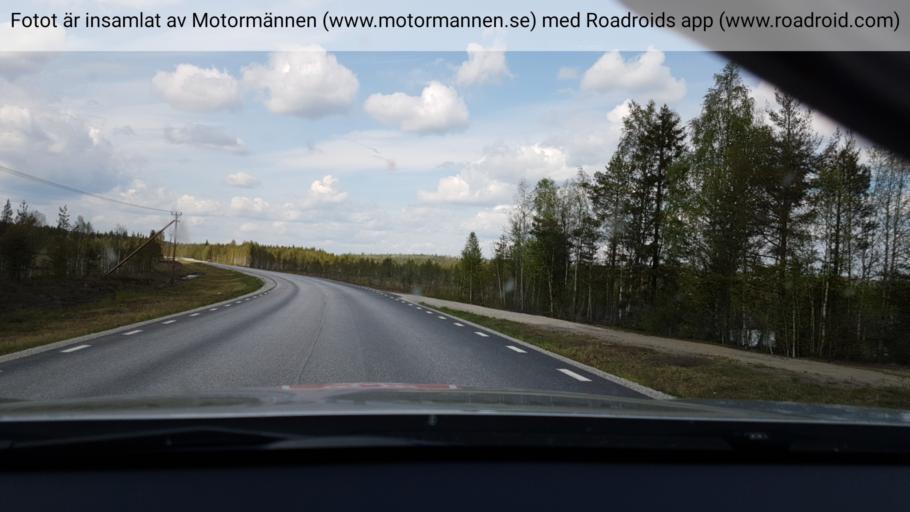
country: SE
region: Vaesterbotten
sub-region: Vannas Kommun
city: Vaennaes
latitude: 64.0386
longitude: 19.6923
